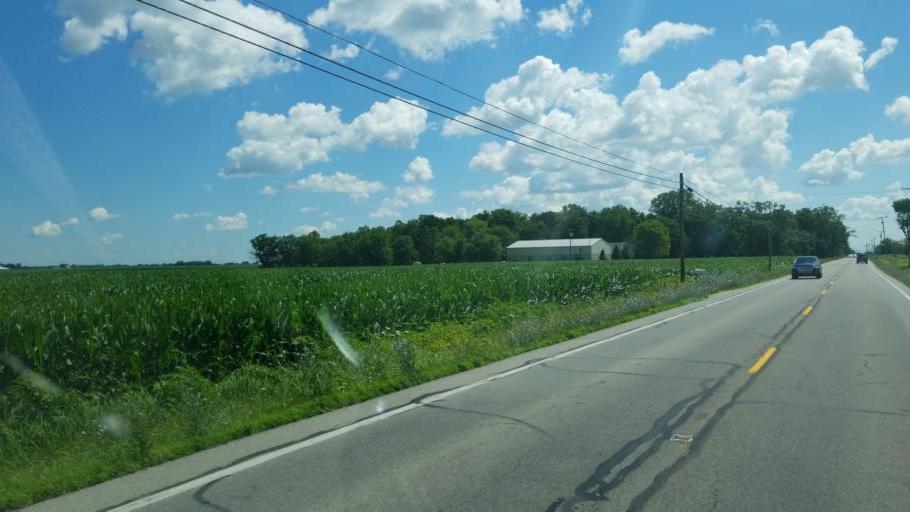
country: US
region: Ohio
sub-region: Marion County
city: Marion
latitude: 40.5818
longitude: -83.0526
